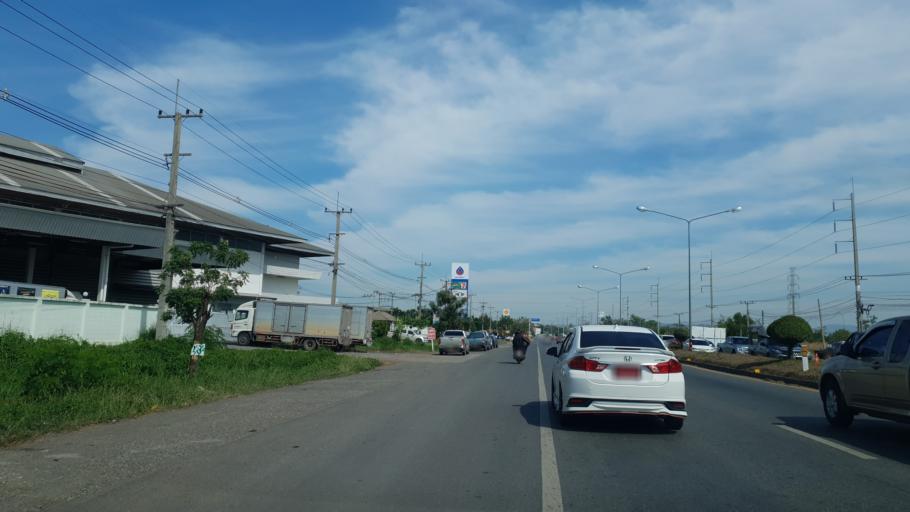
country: TH
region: Phitsanulok
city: Wang Thong
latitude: 16.8556
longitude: 100.3500
